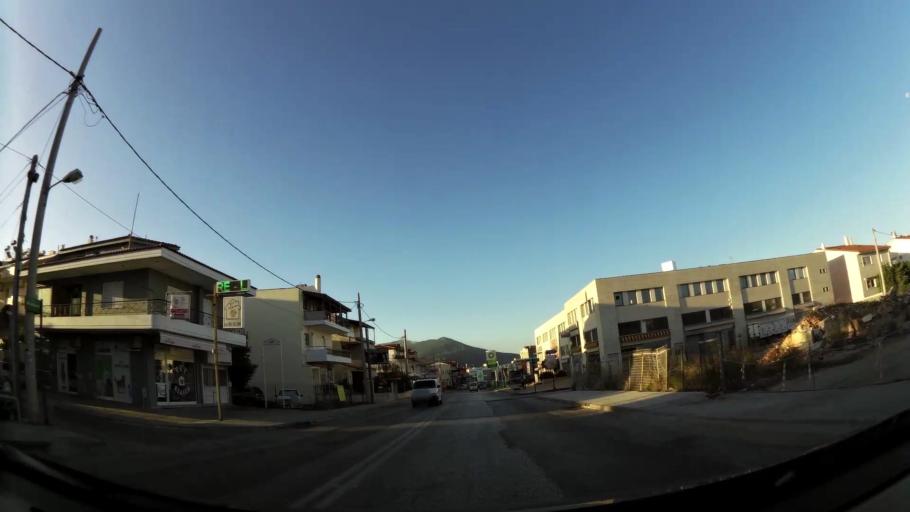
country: GR
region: Attica
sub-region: Nomarchia Anatolikis Attikis
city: Gerakas
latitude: 38.0277
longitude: 23.8515
